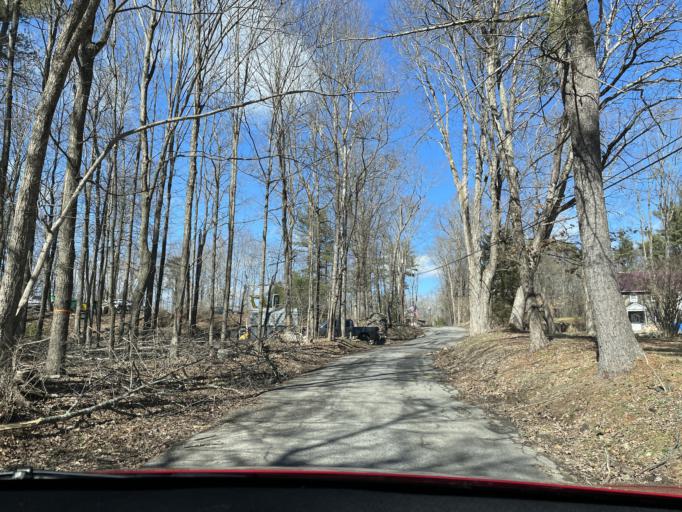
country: US
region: New York
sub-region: Ulster County
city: West Hurley
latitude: 41.9743
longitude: -74.0797
